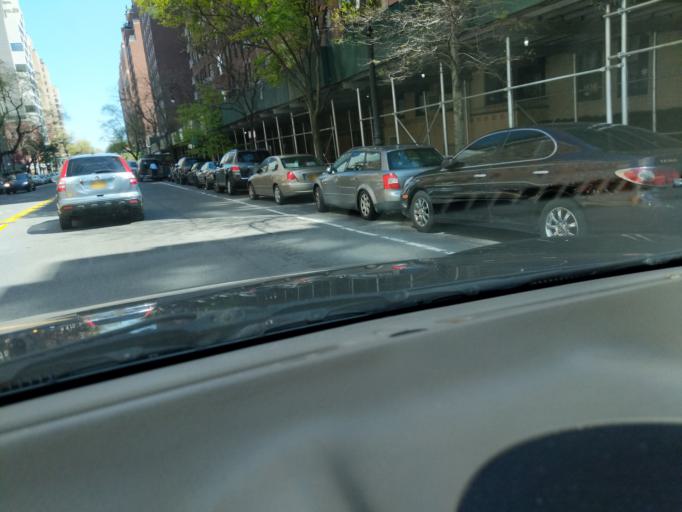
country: US
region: New York
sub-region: New York County
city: Manhattan
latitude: 40.7767
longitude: -73.9487
